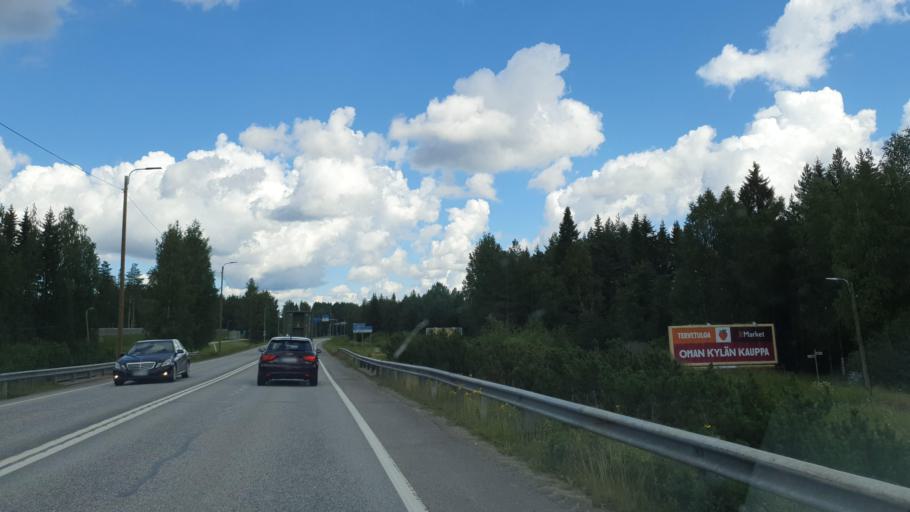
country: FI
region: Kainuu
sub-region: Kajaani
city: Kajaani
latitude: 64.2124
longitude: 27.6617
